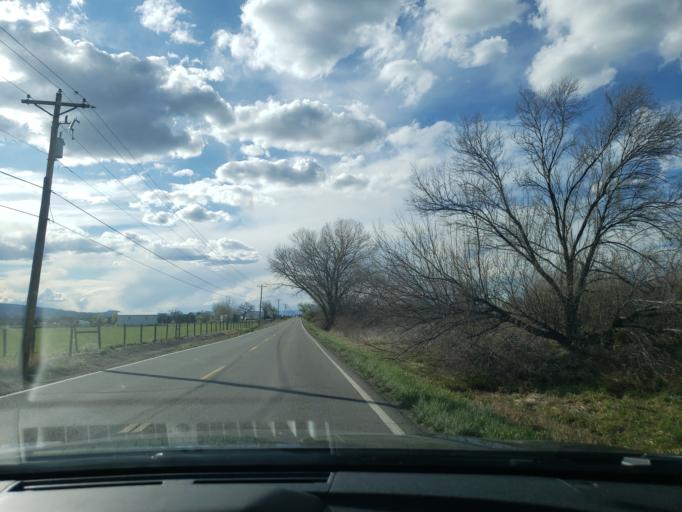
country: US
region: Colorado
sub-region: Mesa County
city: Redlands
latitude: 39.1231
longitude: -108.6716
